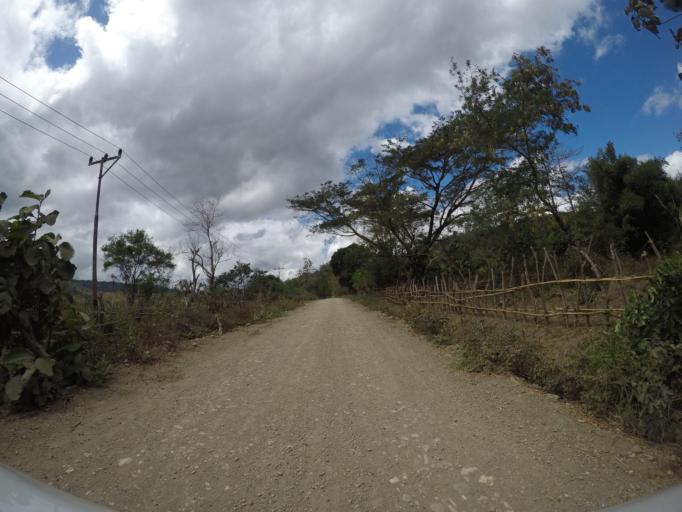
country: TL
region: Lautem
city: Lospalos
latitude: -8.4931
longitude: 126.8236
